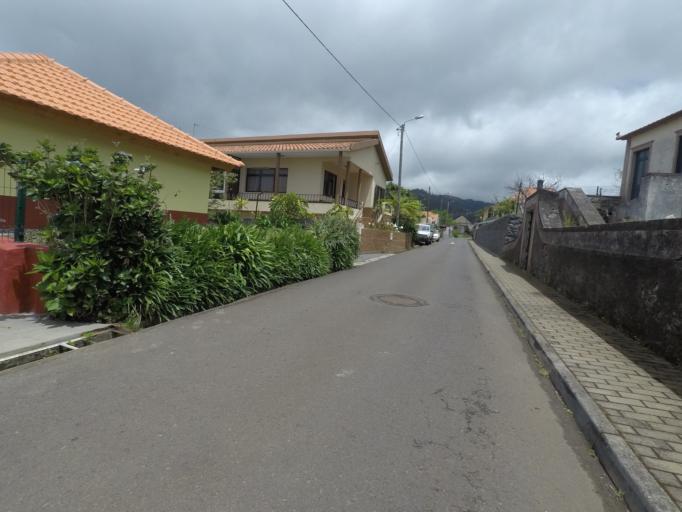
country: PT
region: Madeira
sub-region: Calheta
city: Estreito da Calheta
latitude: 32.7535
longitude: -17.2048
